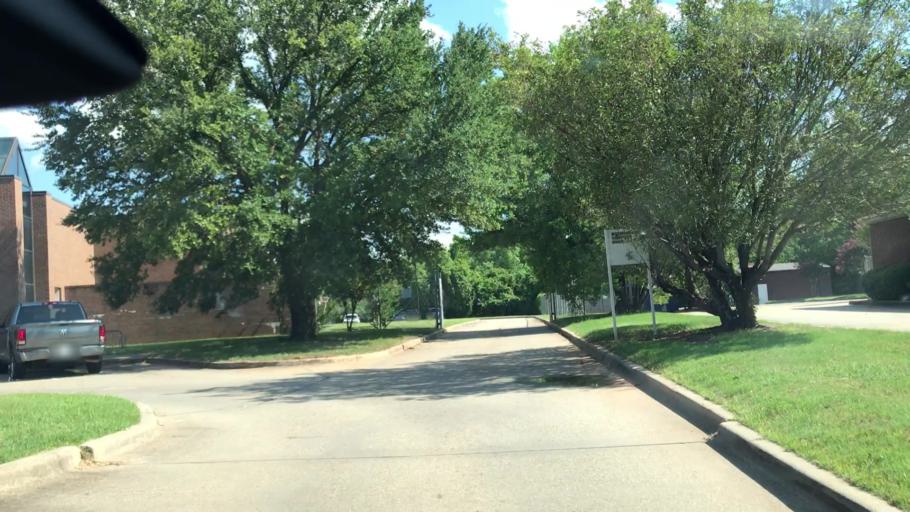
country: US
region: Louisiana
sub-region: Bossier Parish
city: Bossier City
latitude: 32.4432
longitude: -93.7105
